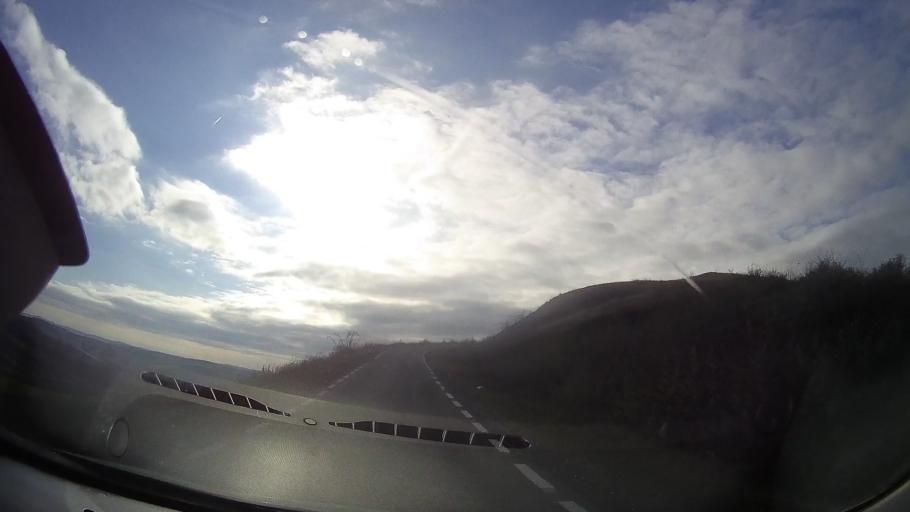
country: RO
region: Mures
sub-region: Comuna Sanger
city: Sanger
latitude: 46.5523
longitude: 24.1607
